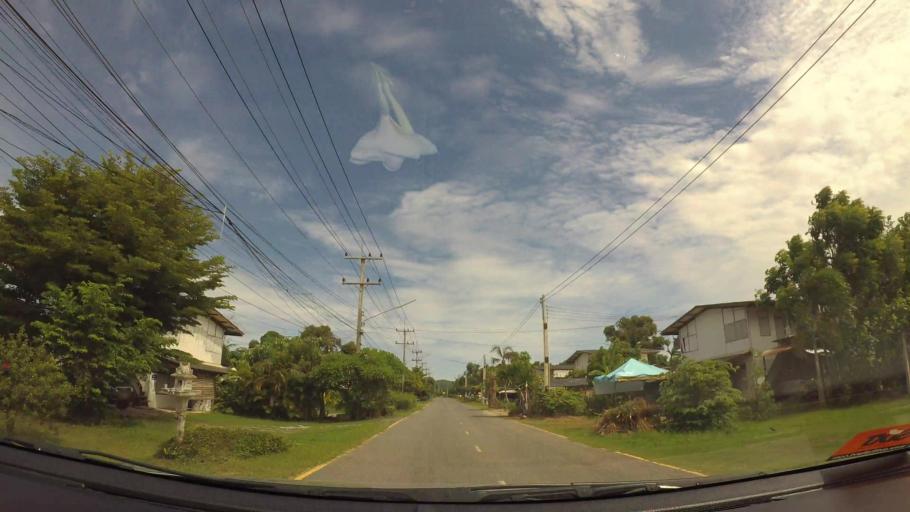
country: TH
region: Chon Buri
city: Sattahip
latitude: 12.6659
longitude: 100.9127
